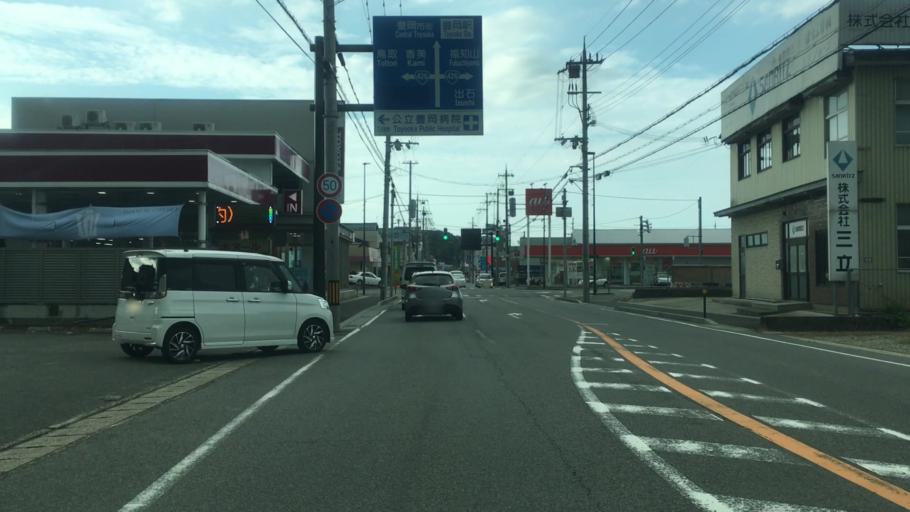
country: JP
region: Hyogo
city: Toyooka
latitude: 35.5275
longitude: 134.8207
